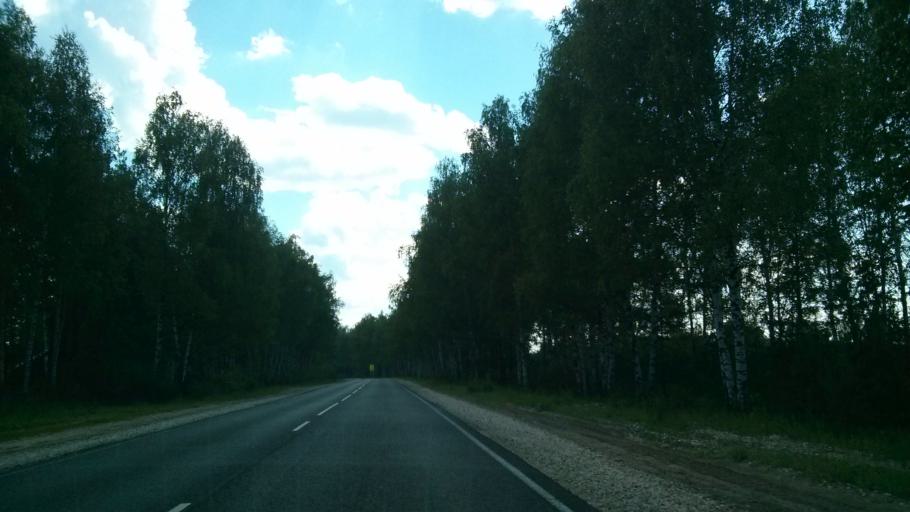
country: RU
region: Vladimir
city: Murom
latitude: 55.5163
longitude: 41.9299
